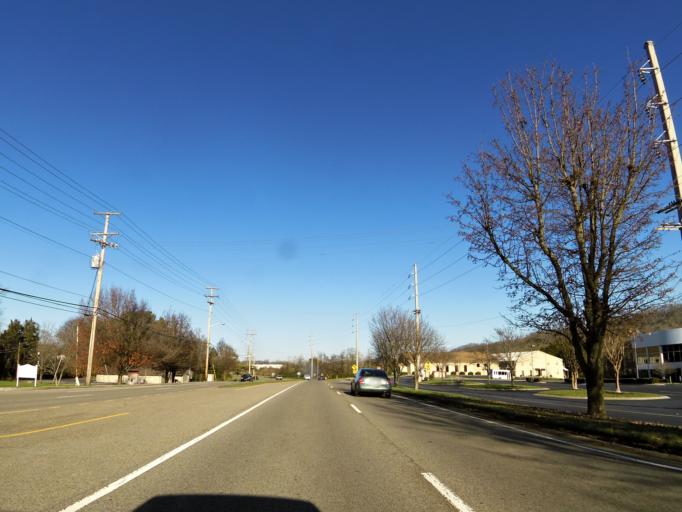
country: US
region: Tennessee
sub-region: Anderson County
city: Oak Ridge
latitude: 36.0324
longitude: -84.2273
